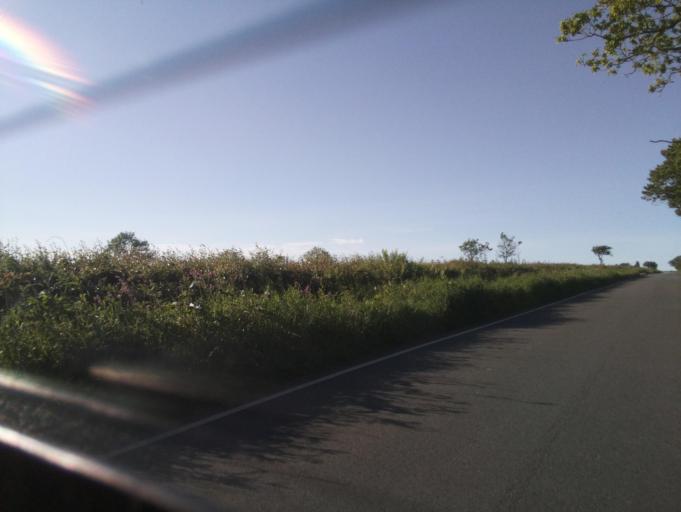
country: GB
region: England
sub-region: Devon
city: Axminster
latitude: 50.7284
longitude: -2.9898
